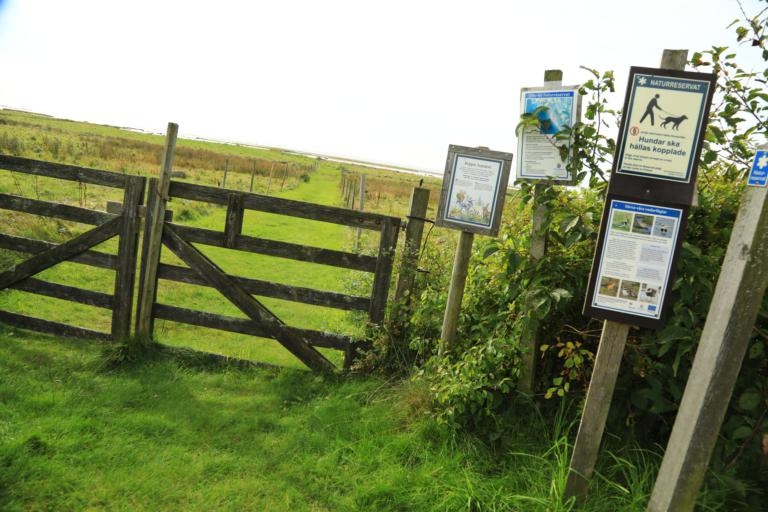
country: SE
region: Halland
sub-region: Varbergs Kommun
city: Traslovslage
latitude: 57.0226
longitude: 12.3361
